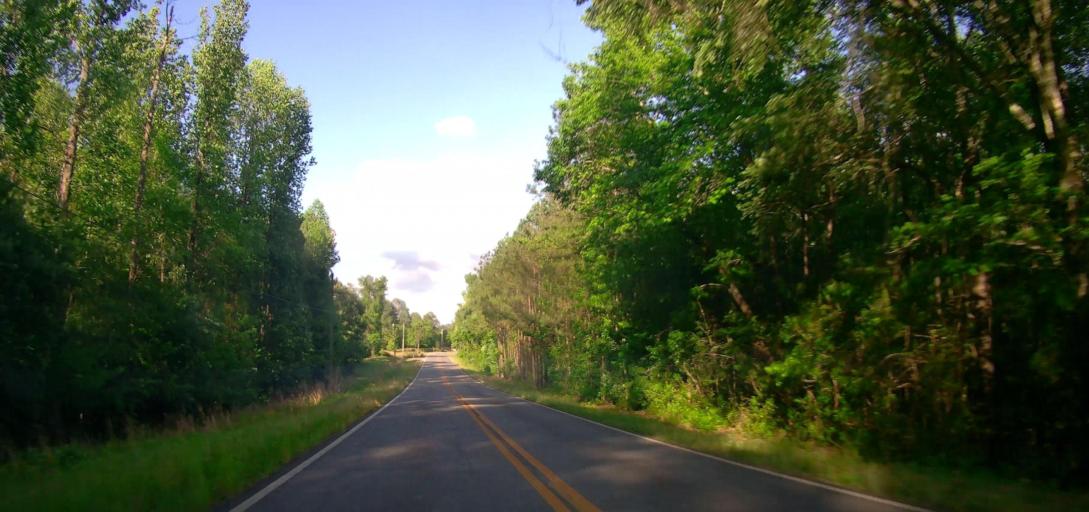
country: US
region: Georgia
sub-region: Peach County
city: Byron
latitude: 32.6773
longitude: -83.7798
